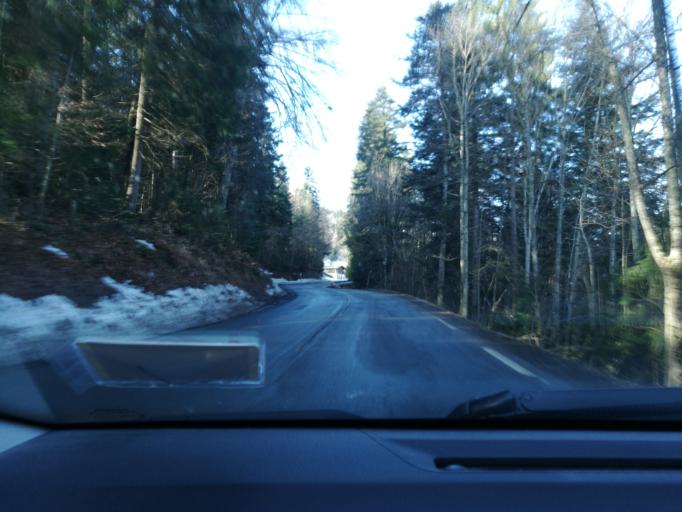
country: FR
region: Rhone-Alpes
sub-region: Departement de la Haute-Savoie
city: Saint-Gervais-les-Bains
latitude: 45.8922
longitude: 6.6880
